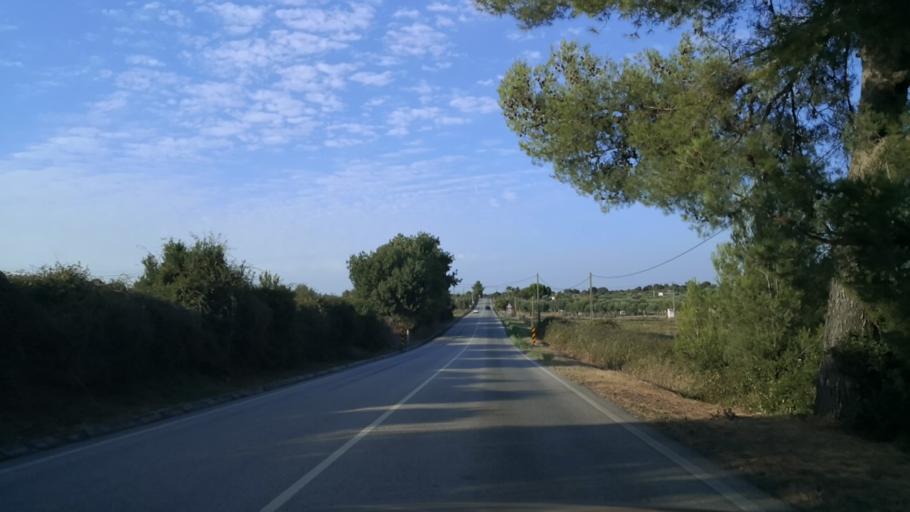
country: PT
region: Santarem
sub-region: Alcanena
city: Alcanena
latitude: 39.3885
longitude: -8.6500
